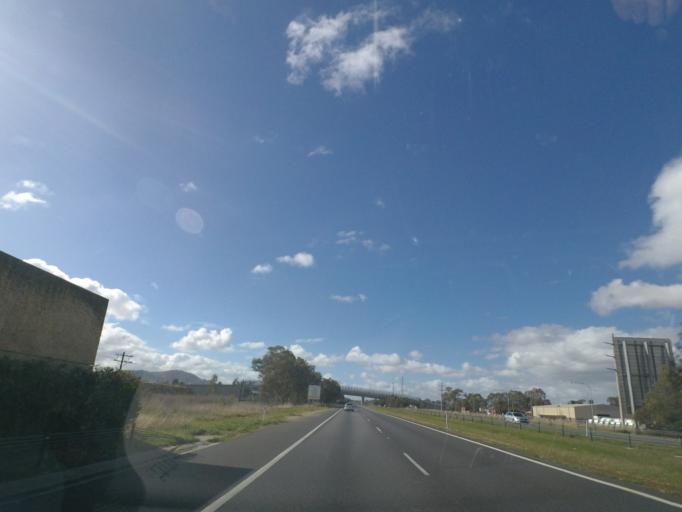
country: AU
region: New South Wales
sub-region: Albury Municipality
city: North Albury
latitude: -36.0661
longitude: 146.9391
